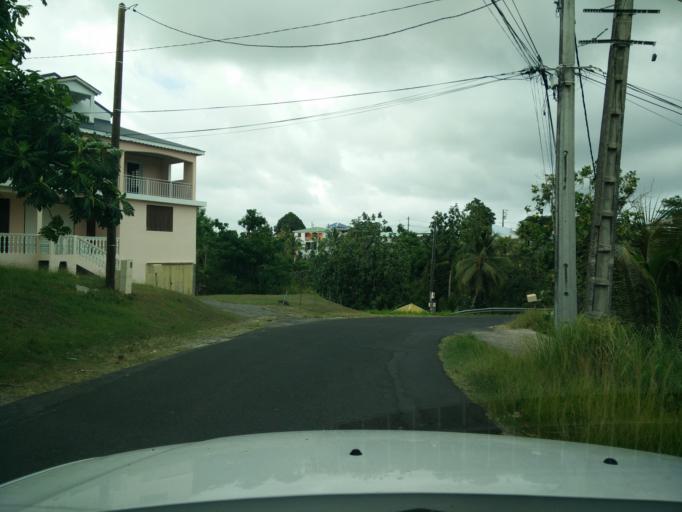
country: GP
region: Guadeloupe
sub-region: Guadeloupe
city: Le Gosier
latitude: 16.2396
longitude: -61.4463
